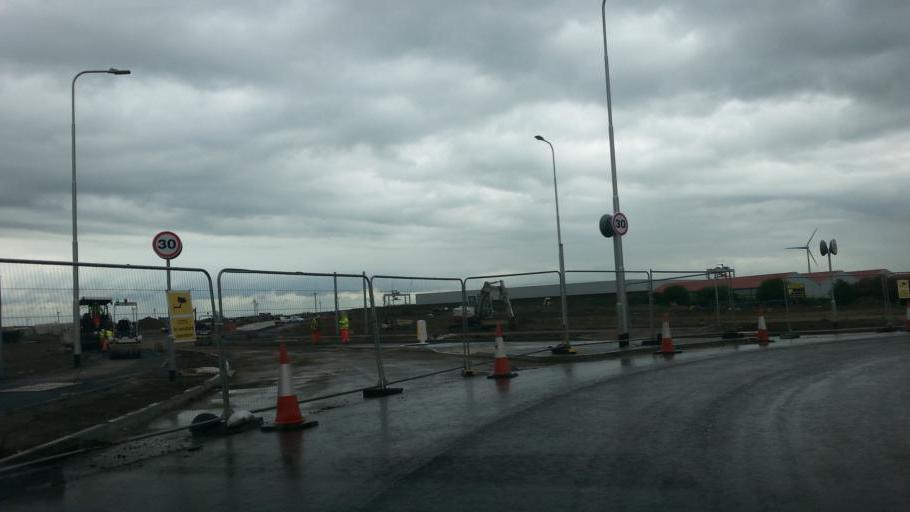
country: GB
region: England
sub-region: Warwickshire
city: Rugby
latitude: 52.3548
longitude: -1.1838
